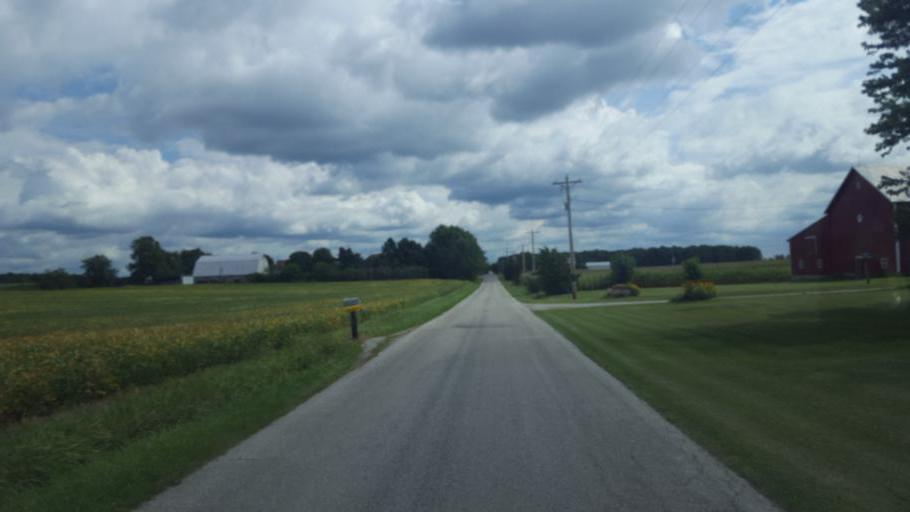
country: US
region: Ohio
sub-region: Sandusky County
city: Mount Carmel
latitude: 41.0957
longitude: -82.9608
